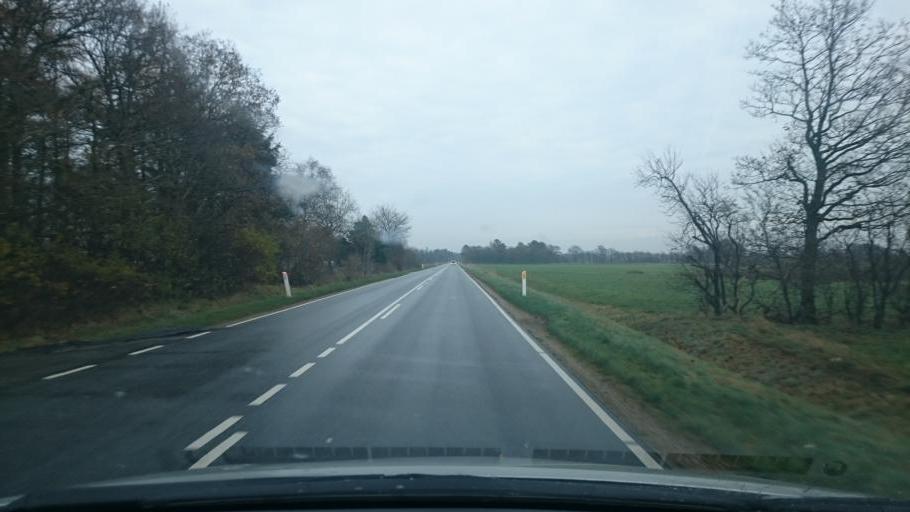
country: DK
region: South Denmark
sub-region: Esbjerg Kommune
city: Ribe
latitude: 55.3351
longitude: 8.8363
